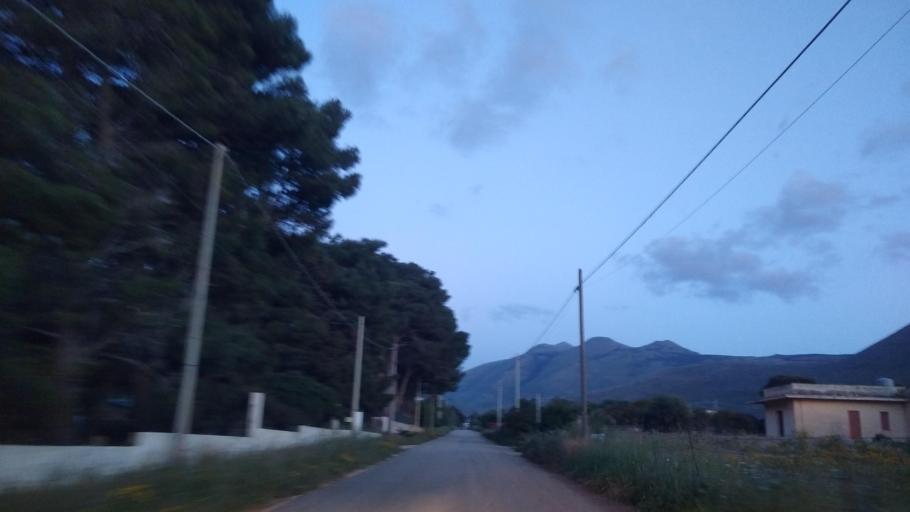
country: IT
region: Sicily
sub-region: Trapani
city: Castelluzzo
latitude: 38.1088
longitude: 12.7266
